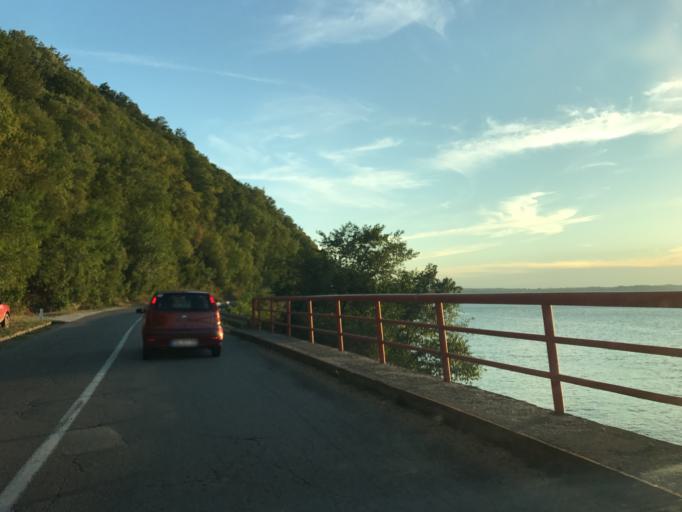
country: RO
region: Caras-Severin
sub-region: Comuna Pescari
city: Coronini
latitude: 44.6587
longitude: 21.6629
